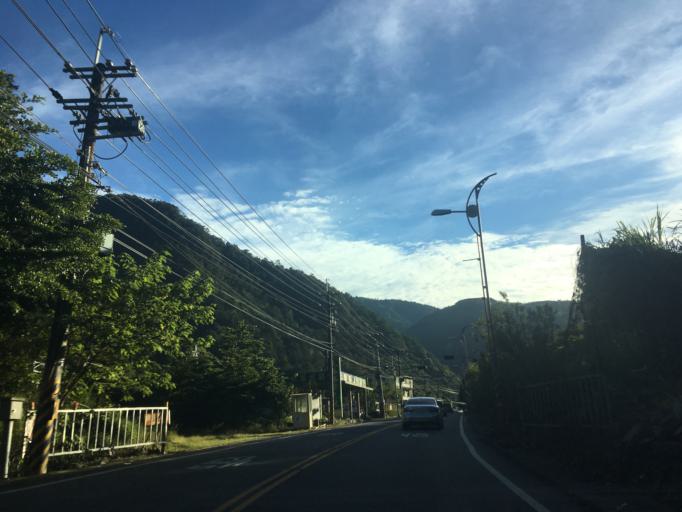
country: TW
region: Taiwan
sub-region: Nantou
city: Puli
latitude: 23.9992
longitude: 121.0802
